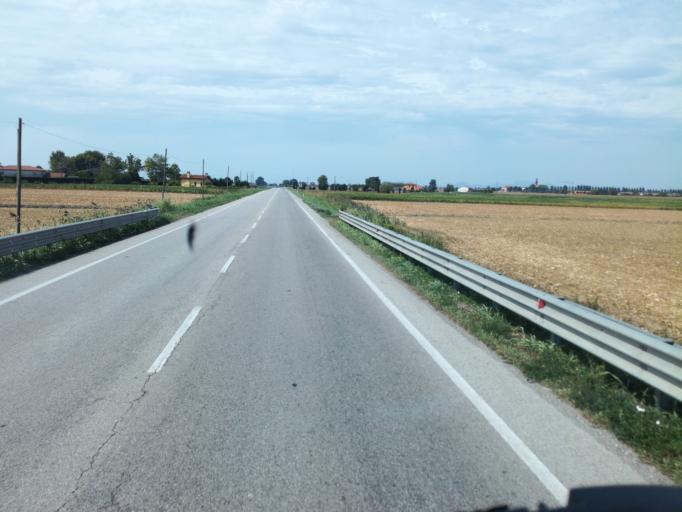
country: IT
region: Veneto
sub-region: Provincia di Padova
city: Candiana
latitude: 45.2135
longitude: 12.0124
